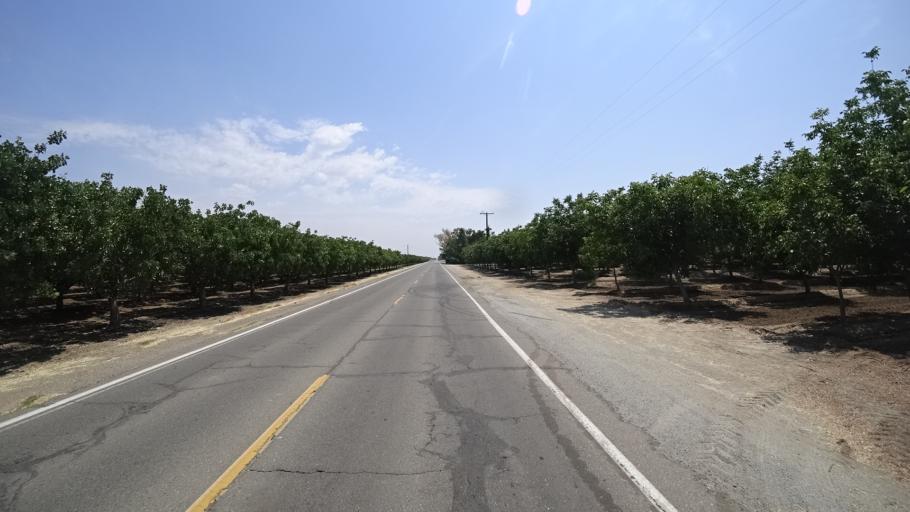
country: US
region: California
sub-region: Kings County
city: Lemoore
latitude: 36.3280
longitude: -119.7697
